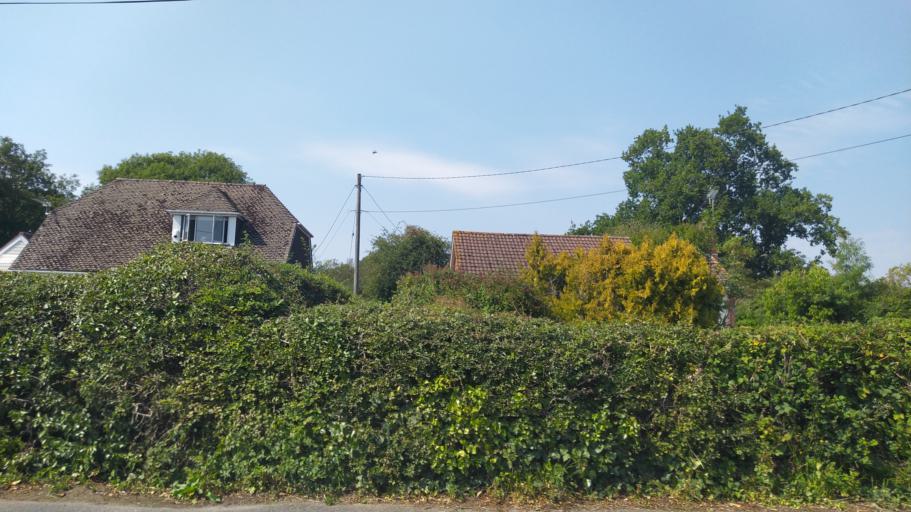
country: GB
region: England
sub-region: Hampshire
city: Cadnam
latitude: 50.9264
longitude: -1.5541
